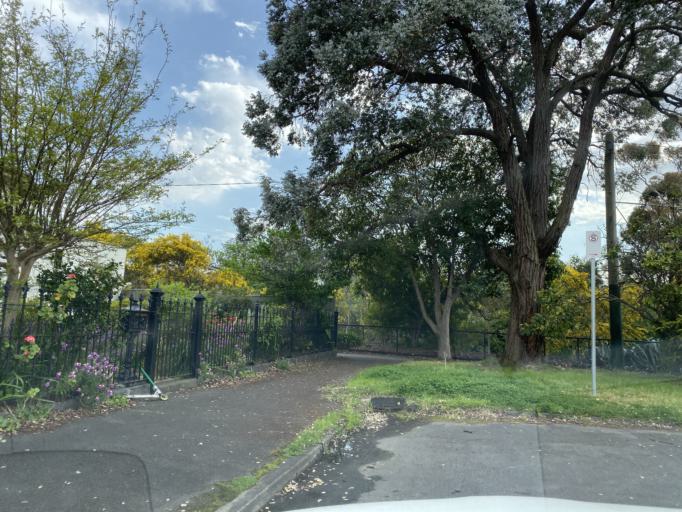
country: AU
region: Victoria
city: Balwyn
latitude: -37.8265
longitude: 145.0678
